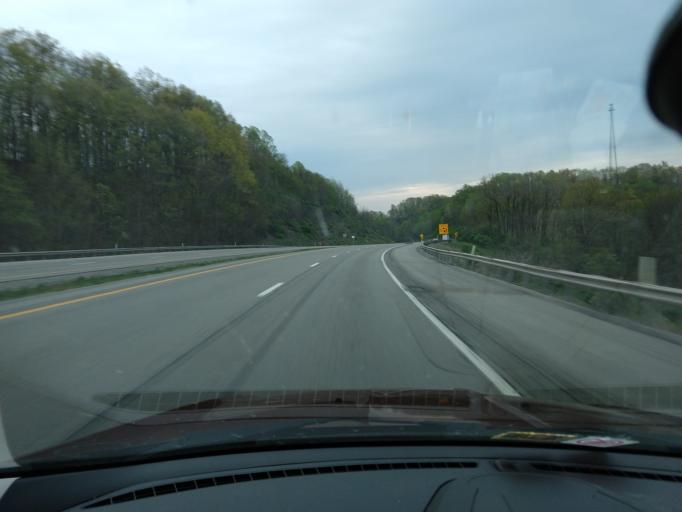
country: US
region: West Virginia
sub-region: Lewis County
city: Weston
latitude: 38.9605
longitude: -80.5252
